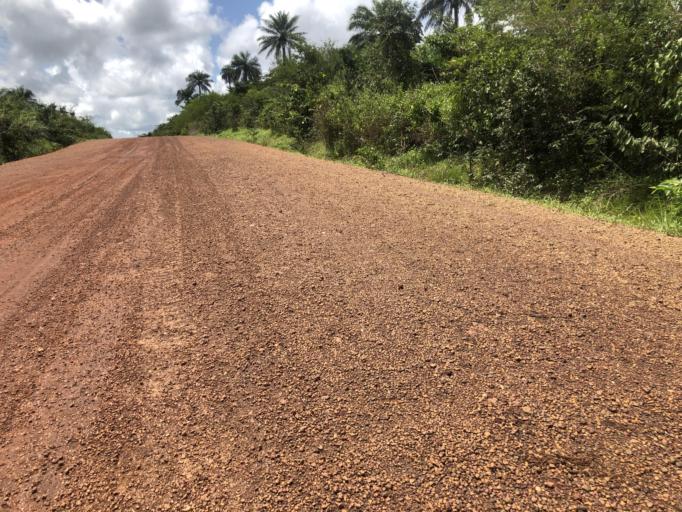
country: SL
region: Northern Province
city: Port Loko
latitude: 8.7164
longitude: -12.8441
